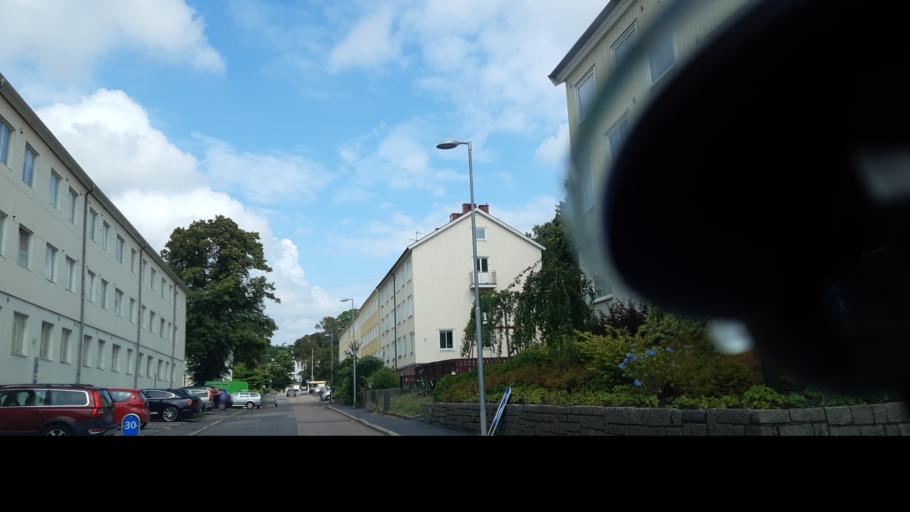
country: SE
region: Vaestra Goetaland
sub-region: Goteborg
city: Eriksbo
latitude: 57.7163
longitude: 12.0346
